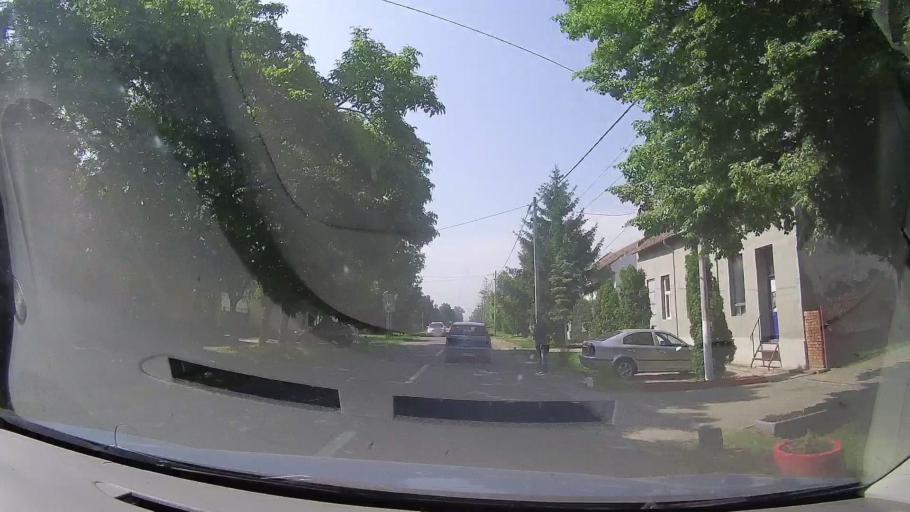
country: RS
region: Autonomna Pokrajina Vojvodina
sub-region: Srednjebanatski Okrug
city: Secanj
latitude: 45.3658
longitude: 20.7723
